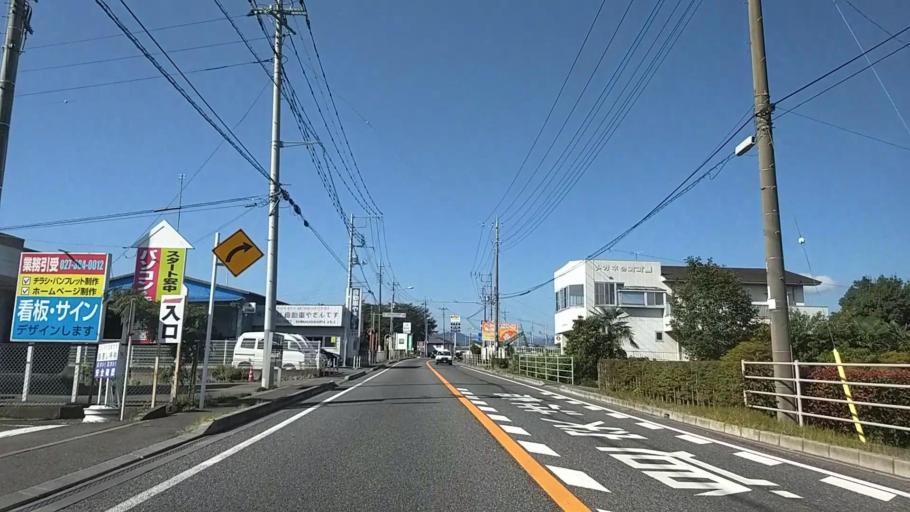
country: JP
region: Gunma
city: Annaka
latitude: 36.3150
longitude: 138.8670
